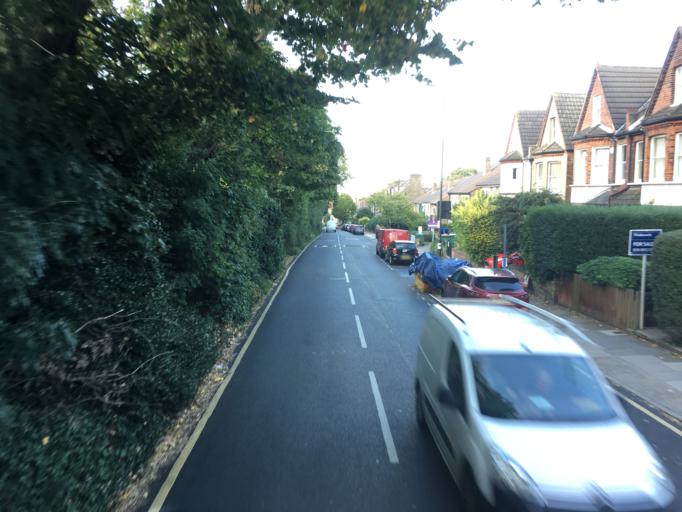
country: GB
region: England
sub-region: Greater London
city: Blackheath
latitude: 51.4790
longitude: 0.0193
